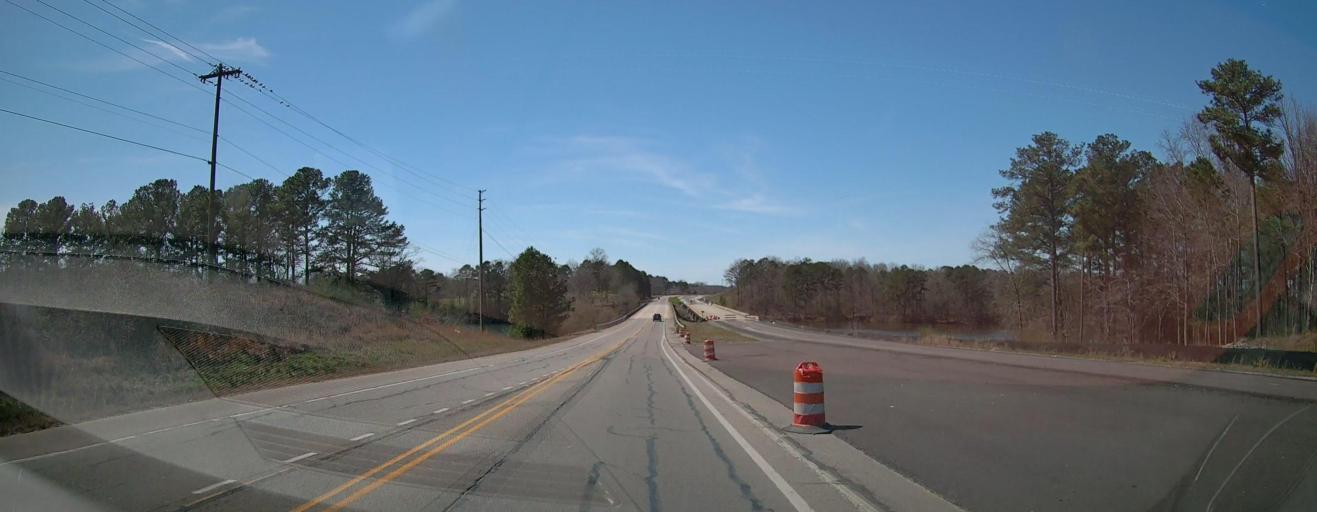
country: US
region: Alabama
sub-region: Cullman County
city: Cullman
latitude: 34.1987
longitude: -86.8089
